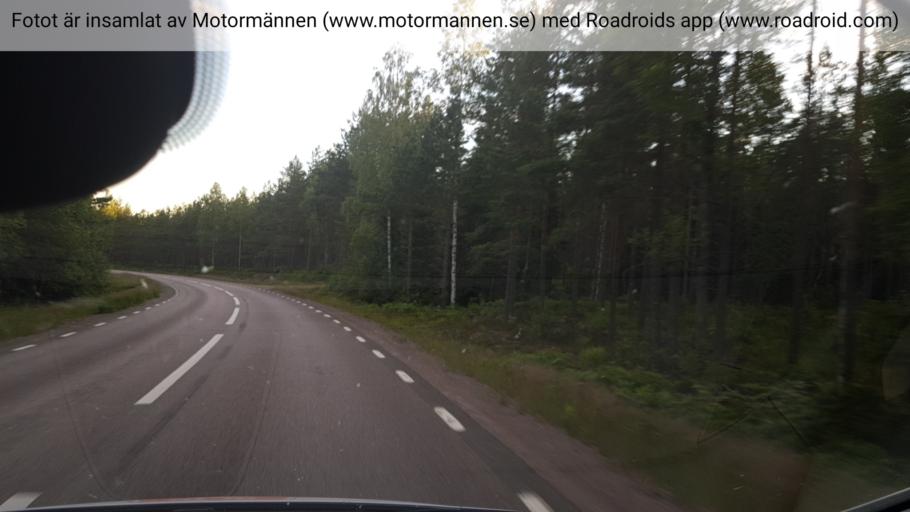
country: SE
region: Vaermland
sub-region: Sunne Kommun
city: Sunne
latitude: 59.6898
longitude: 13.0509
